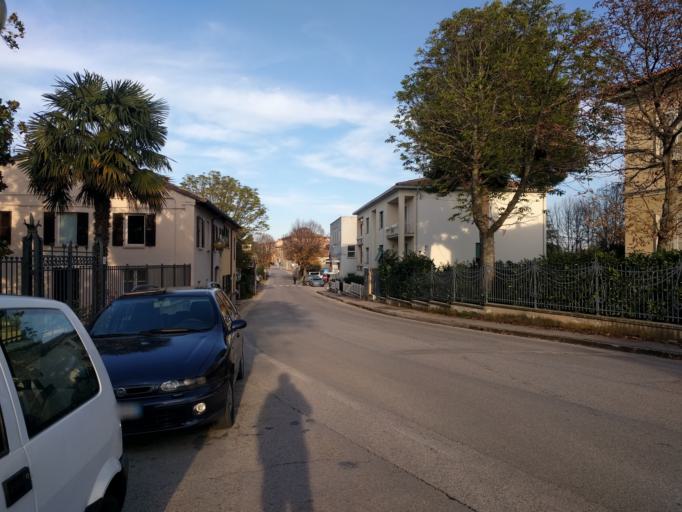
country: IT
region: The Marches
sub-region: Provincia di Ancona
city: Ostra
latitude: 43.6105
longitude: 13.1535
